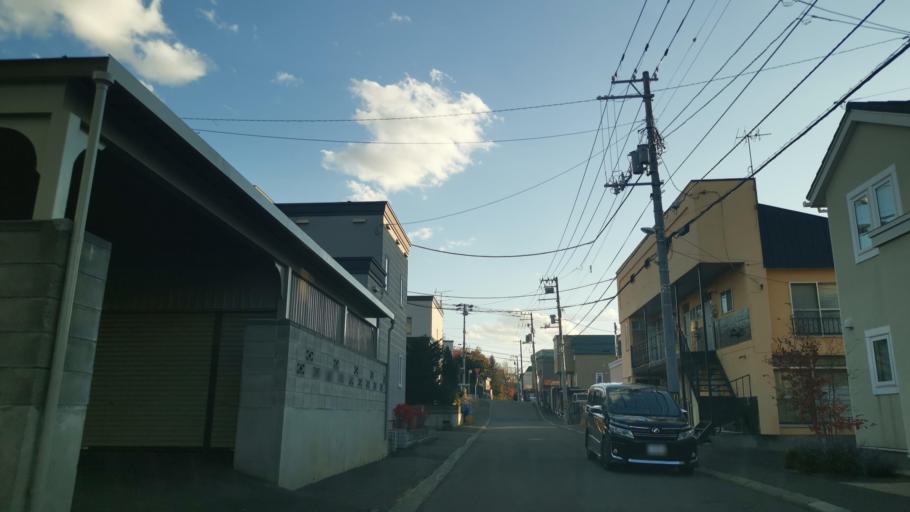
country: JP
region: Hokkaido
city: Sapporo
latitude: 43.0016
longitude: 141.3665
